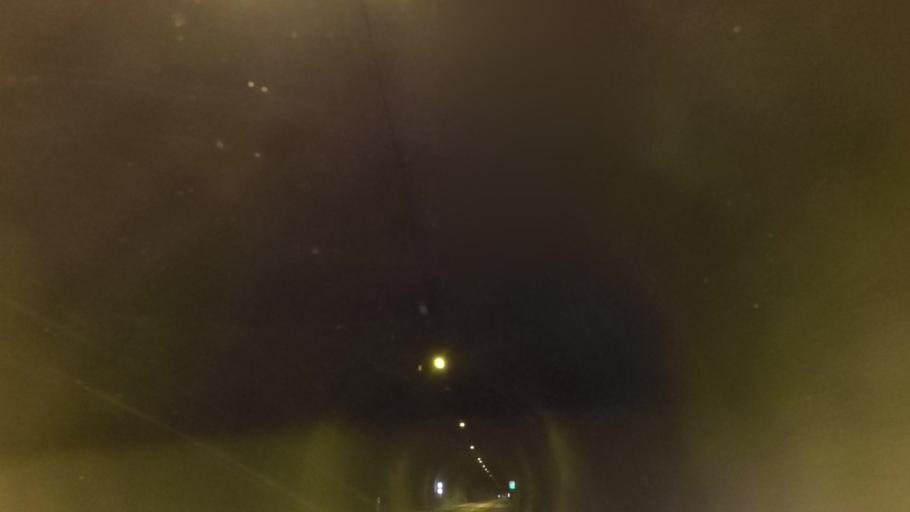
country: IS
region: Westfjords
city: Isafjoerdur
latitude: 66.1323
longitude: -23.1800
